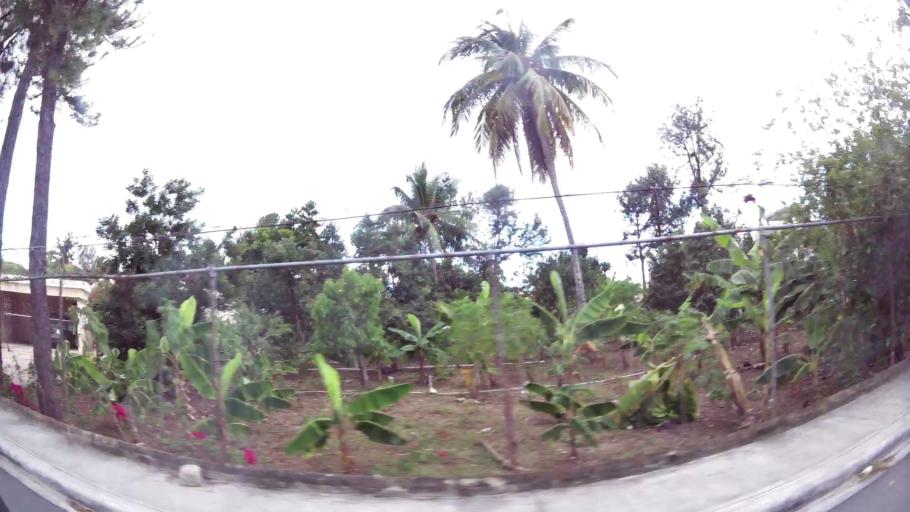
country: DO
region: San Cristobal
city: San Cristobal
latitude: 18.4202
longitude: -70.0933
